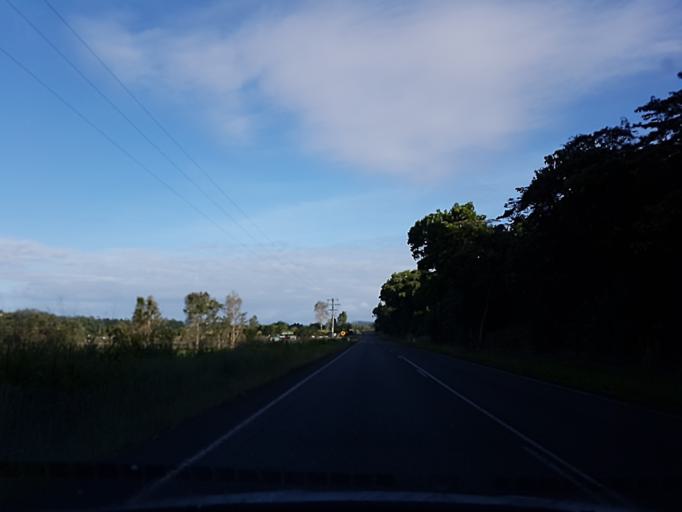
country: AU
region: Queensland
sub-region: Cairns
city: Port Douglas
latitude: -16.3258
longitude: 145.4088
